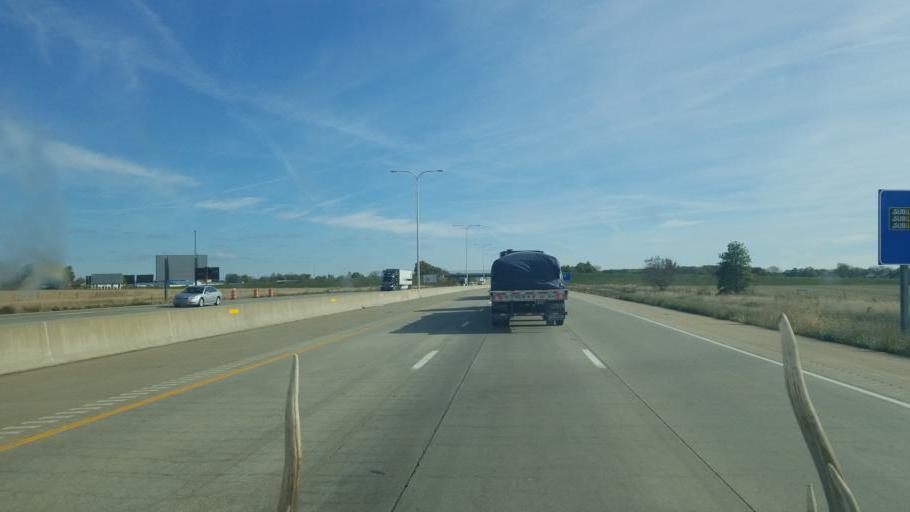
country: US
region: Illinois
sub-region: Effingham County
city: Effingham
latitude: 39.1428
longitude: -88.5468
